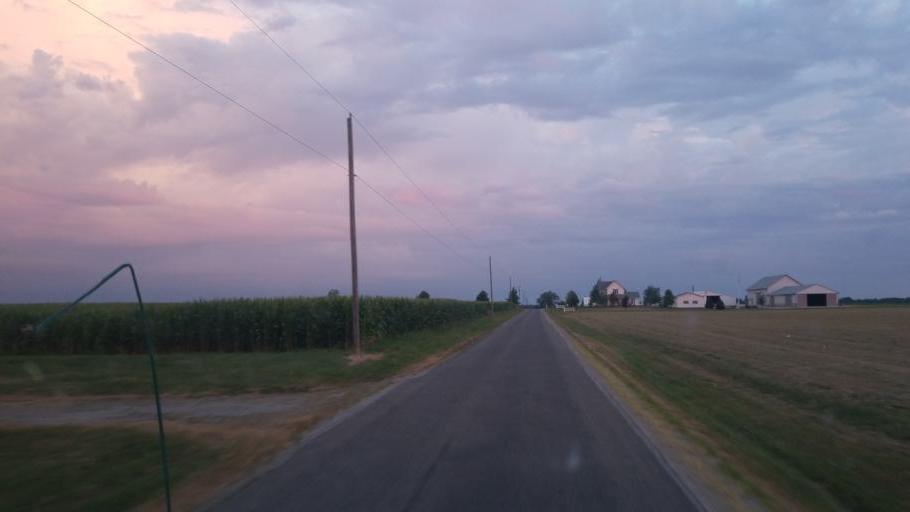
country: US
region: Ohio
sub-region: Defiance County
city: Hicksville
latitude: 41.3536
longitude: -84.7920
